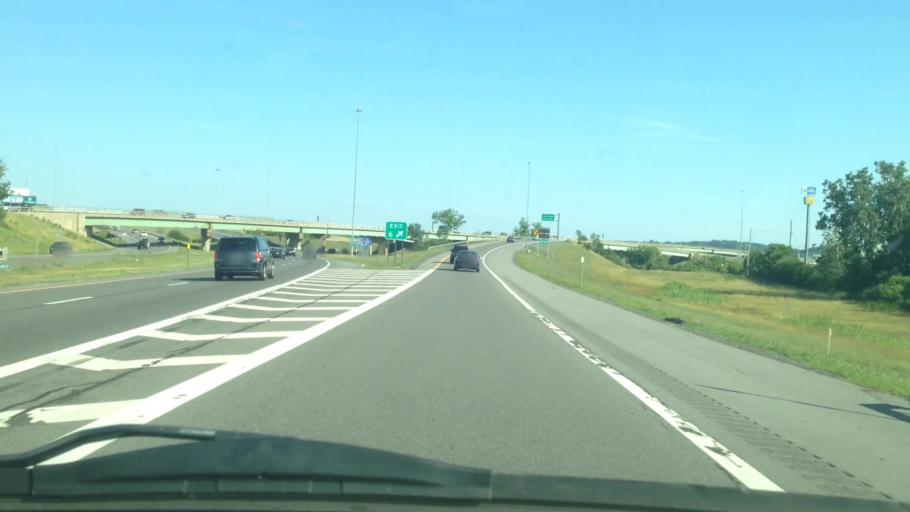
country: US
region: New York
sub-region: Onondaga County
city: Lakeland
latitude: 43.0847
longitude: -76.2287
